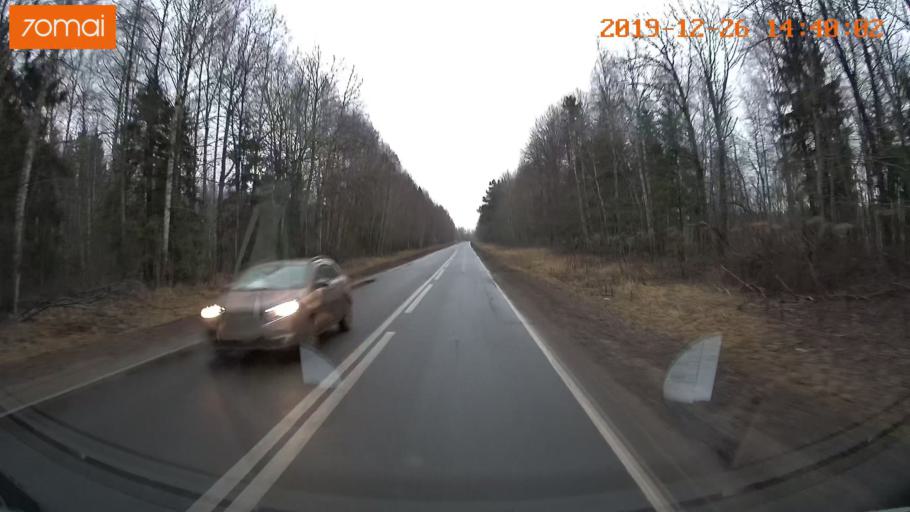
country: RU
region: Jaroslavl
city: Poshekhon'ye
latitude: 58.3784
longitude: 38.9902
